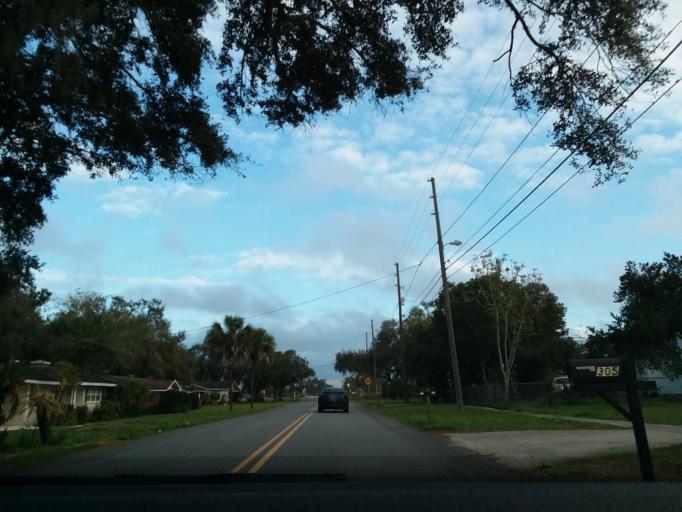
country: US
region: Florida
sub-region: Polk County
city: Haines City
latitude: 28.1097
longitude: -81.6481
